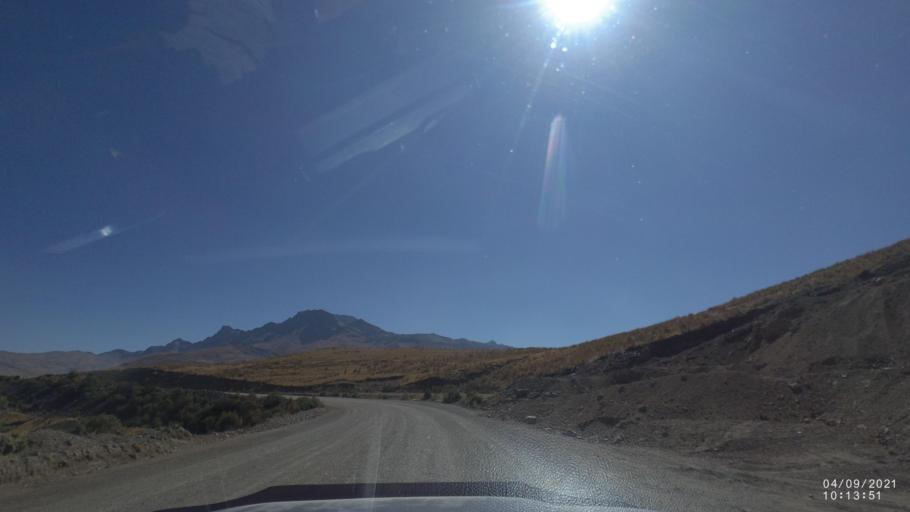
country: BO
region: Cochabamba
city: Sipe Sipe
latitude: -17.3341
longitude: -66.4059
